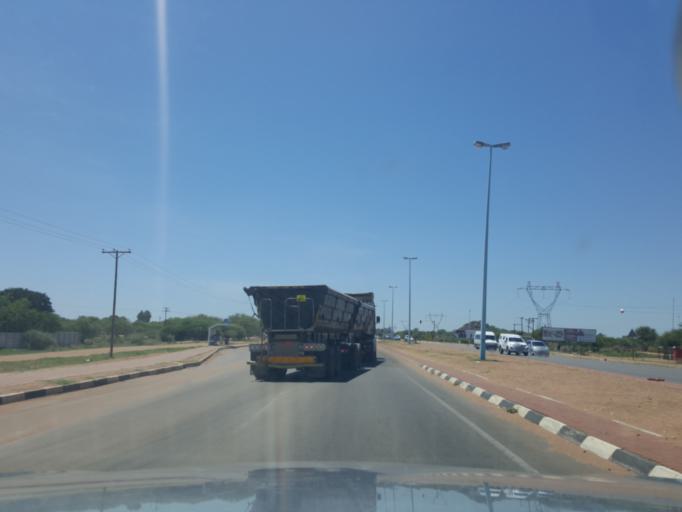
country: BW
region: Kweneng
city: Gaphatshwe
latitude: -24.5887
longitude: 25.8448
